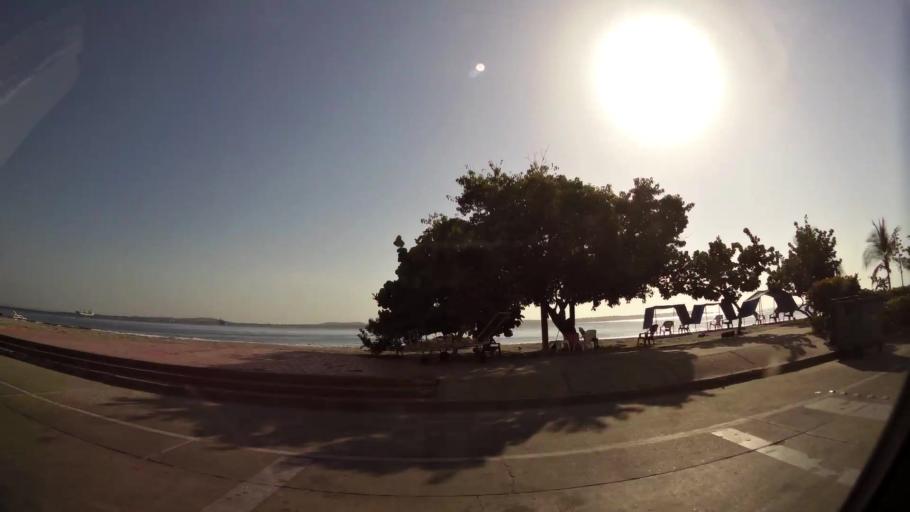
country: CO
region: Bolivar
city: Cartagena
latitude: 10.3923
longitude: -75.5500
